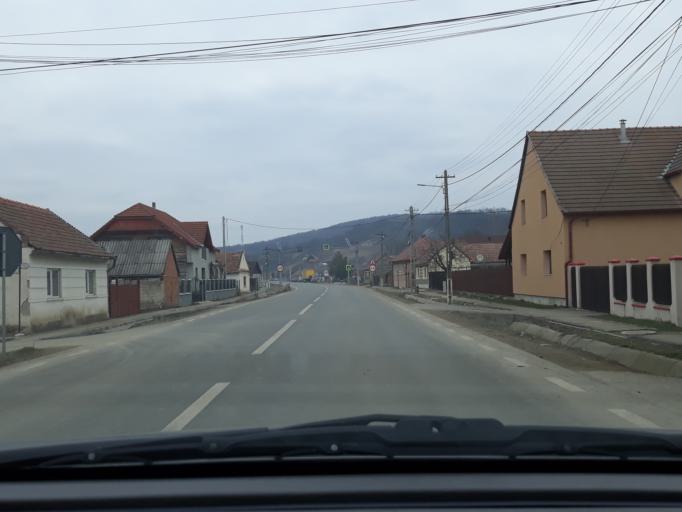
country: RO
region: Salaj
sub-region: Comuna Nusfalau
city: Nusfalau
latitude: 47.2020
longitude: 22.7136
